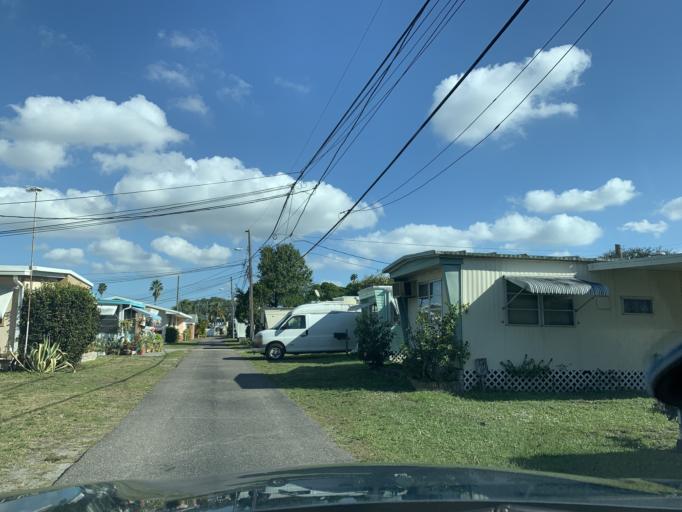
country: US
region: Florida
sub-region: Pinellas County
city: Belleair
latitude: 27.9263
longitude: -82.7982
